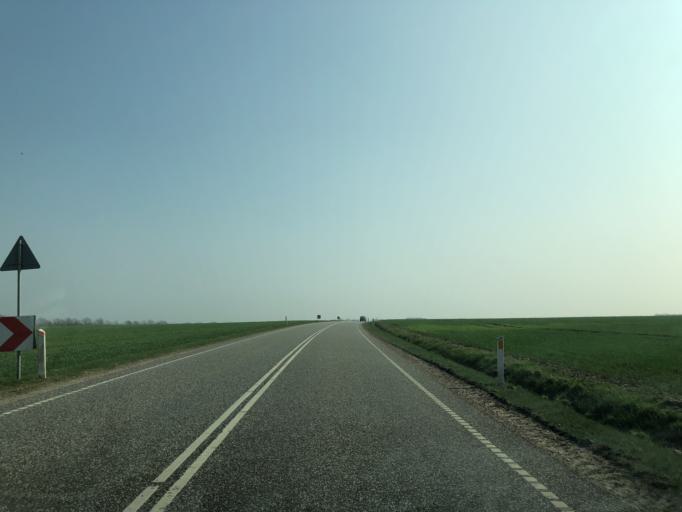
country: DK
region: Central Jutland
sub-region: Ringkobing-Skjern Kommune
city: Skjern
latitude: 56.0510
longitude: 8.5041
